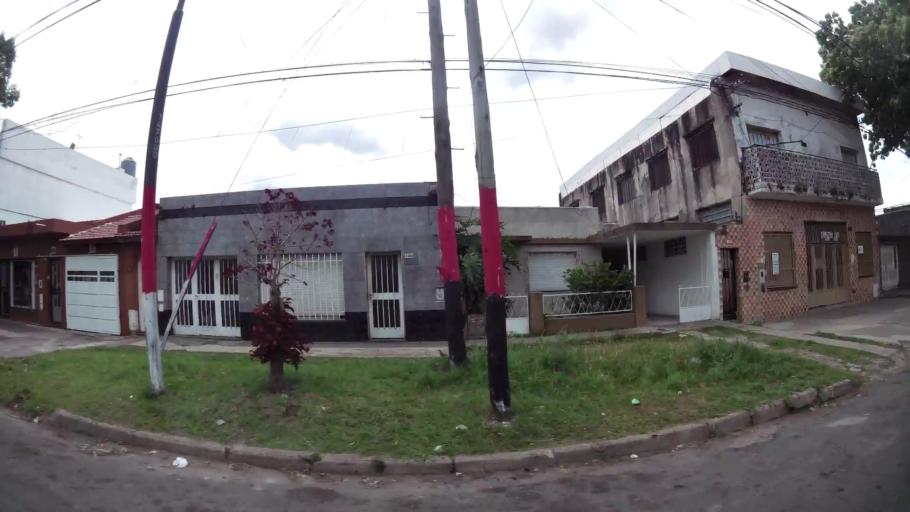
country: AR
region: Santa Fe
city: Gobernador Galvez
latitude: -33.0000
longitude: -60.6543
